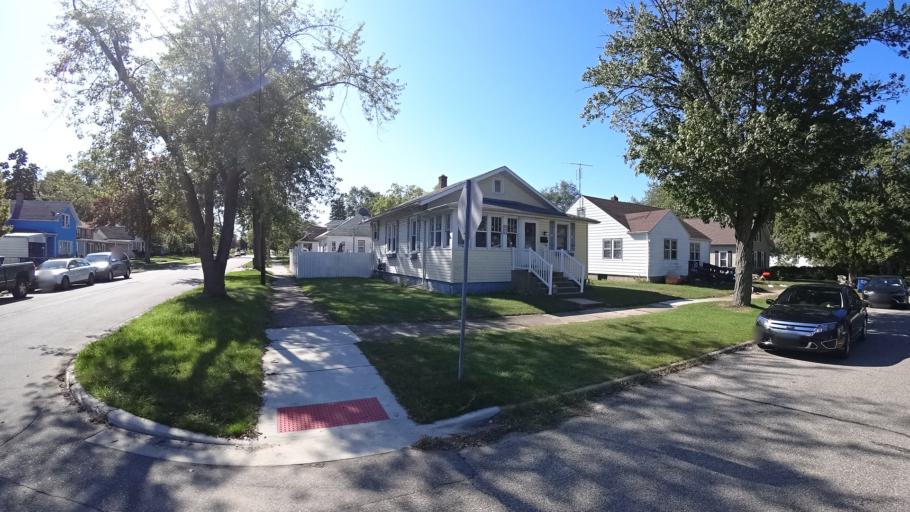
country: US
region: Indiana
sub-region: LaPorte County
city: Michigan City
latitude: 41.7075
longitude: -86.8846
